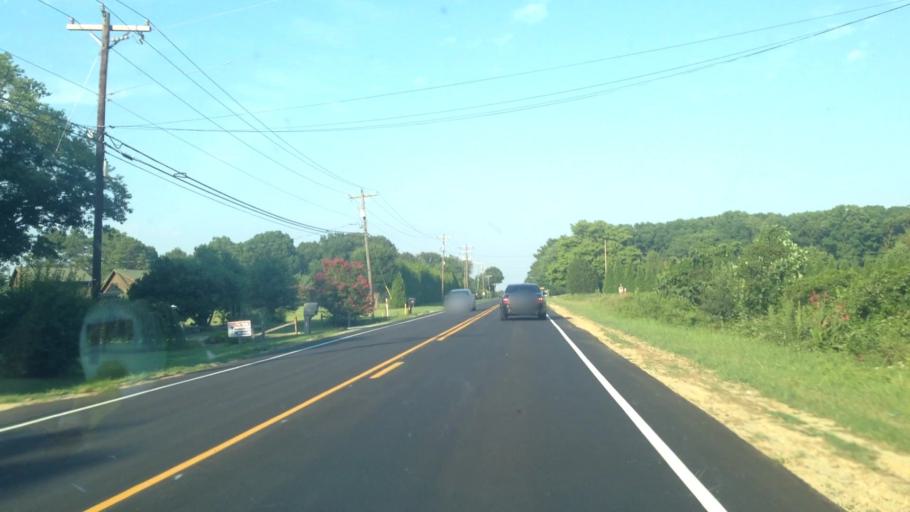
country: US
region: North Carolina
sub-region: Guilford County
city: Summerfield
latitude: 36.2496
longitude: -79.9114
